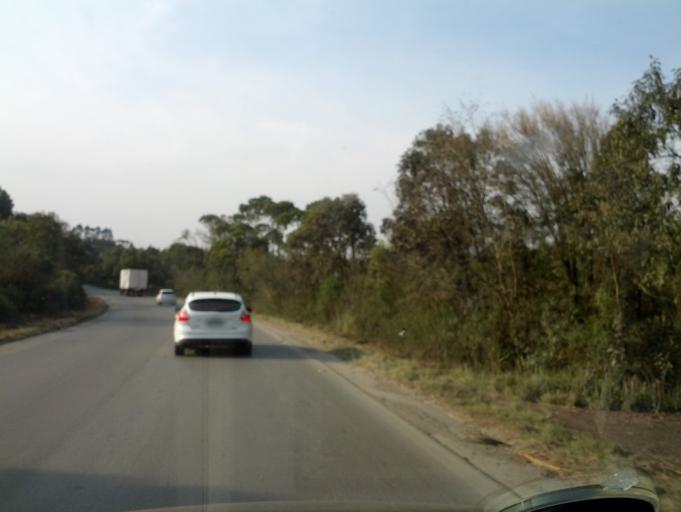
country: BR
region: Santa Catarina
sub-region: Otacilio Costa
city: Otacilio Costa
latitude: -27.5526
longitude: -50.1475
